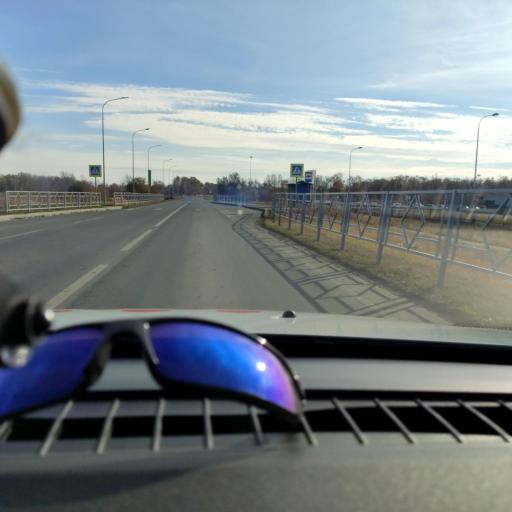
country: RU
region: Samara
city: Samara
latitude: 53.0875
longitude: 50.1380
